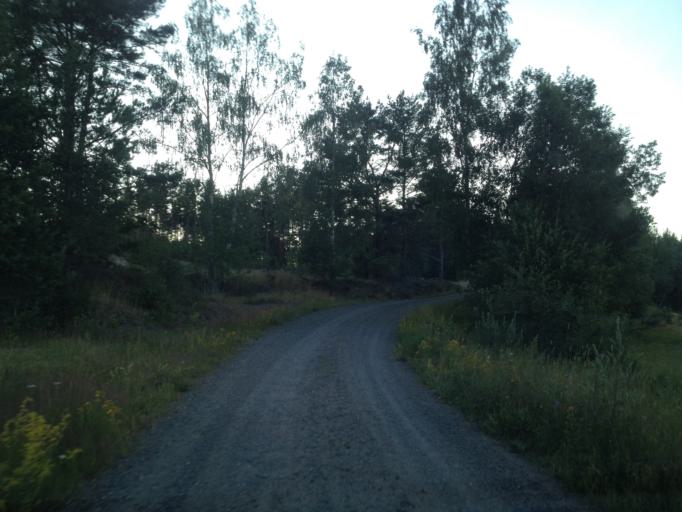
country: SE
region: Kalmar
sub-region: Vasterviks Kommun
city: Overum
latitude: 58.0214
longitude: 16.1183
